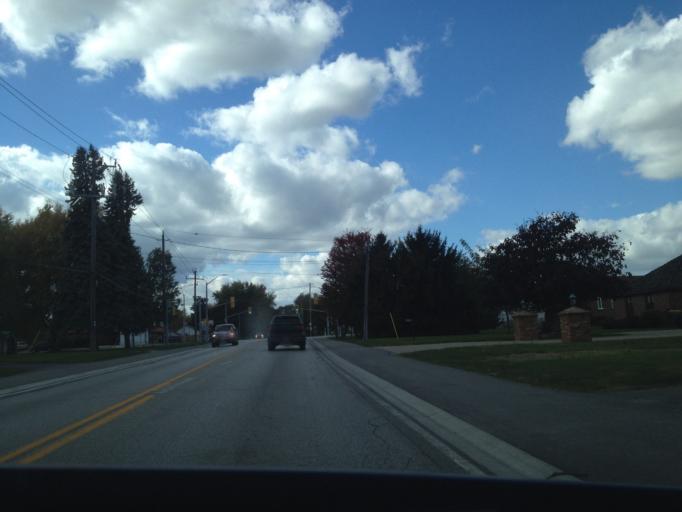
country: CA
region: Ontario
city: Amherstburg
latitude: 42.0397
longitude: -82.6712
